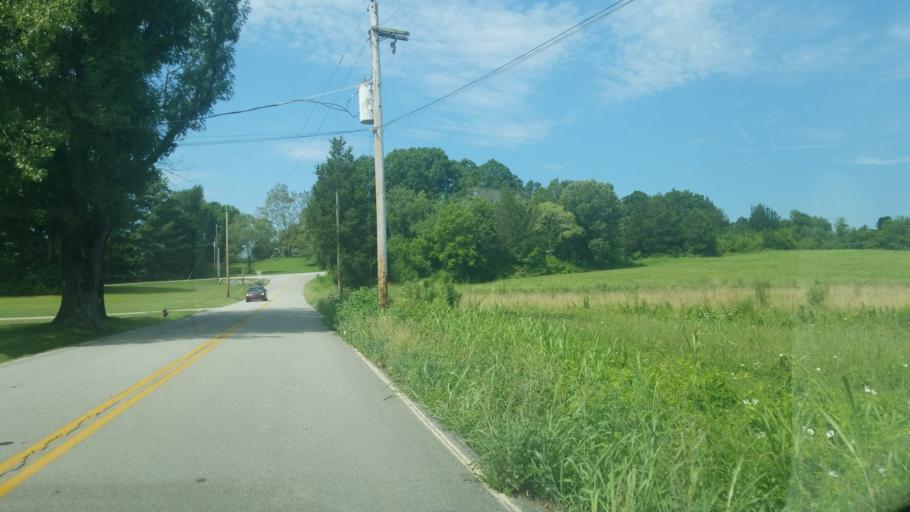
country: US
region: Tennessee
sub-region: Hamilton County
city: Lakesite
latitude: 35.1794
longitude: -85.0448
